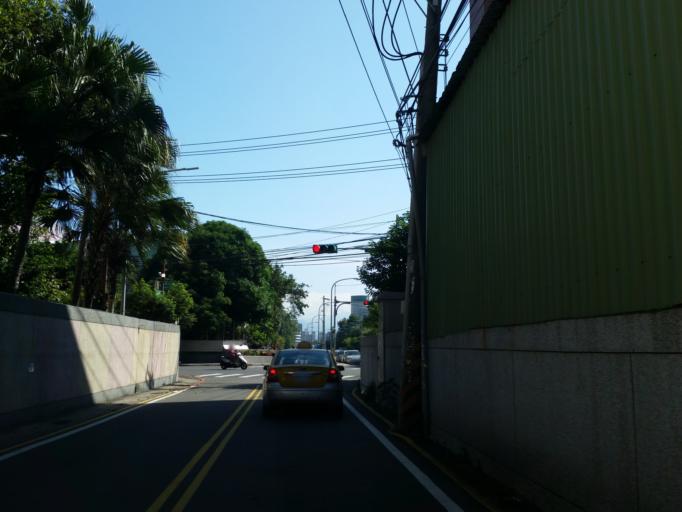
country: TW
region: Taiwan
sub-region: Taoyuan
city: Taoyuan
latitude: 24.9866
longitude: 121.3217
